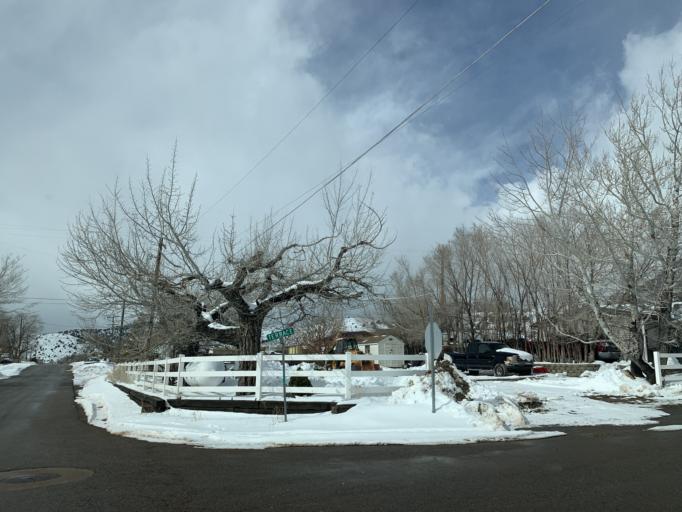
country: US
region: Utah
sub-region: Utah County
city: Genola
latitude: 39.9579
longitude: -112.1083
